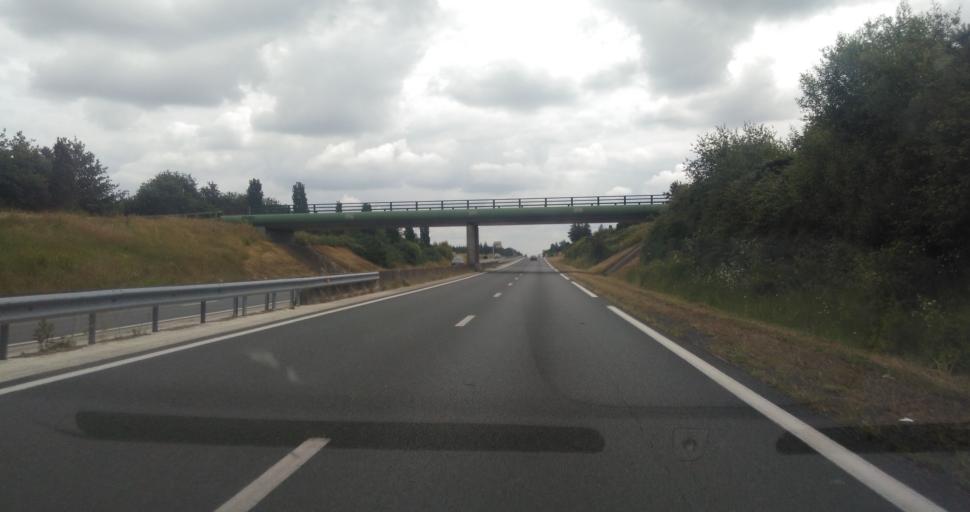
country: FR
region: Pays de la Loire
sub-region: Departement de la Vendee
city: La Chaize-le-Vicomte
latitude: 46.6533
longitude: -1.2316
